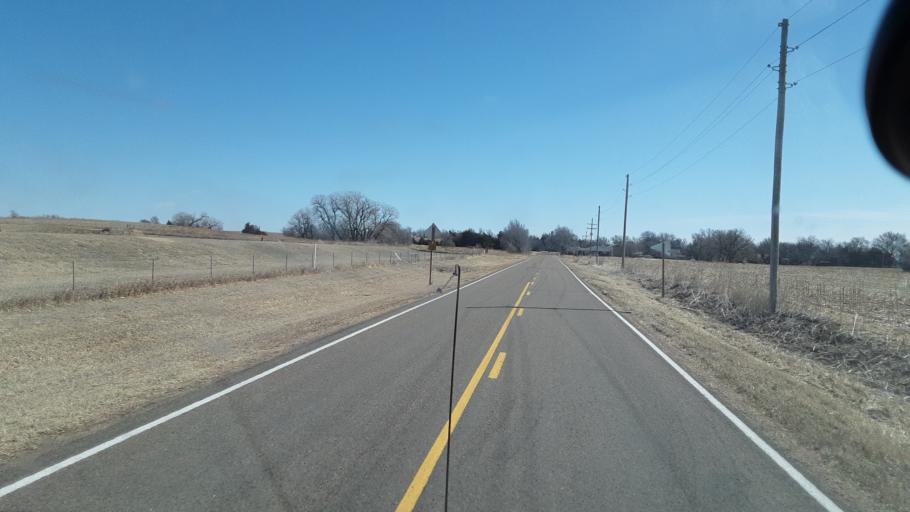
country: US
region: Kansas
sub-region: Barton County
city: Ellinwood
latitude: 38.2820
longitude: -98.4225
